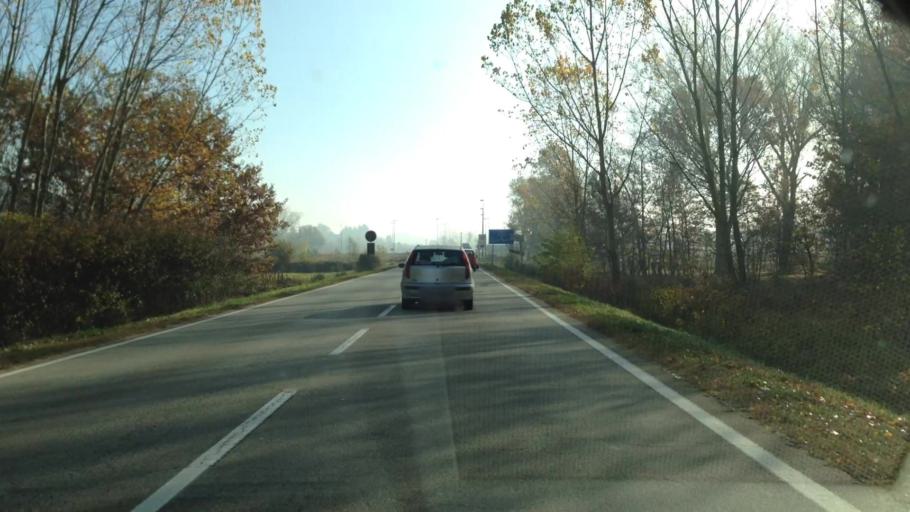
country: IT
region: Piedmont
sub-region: Provincia di Asti
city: Vigliano d'Asti
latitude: 44.8236
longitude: 8.2216
